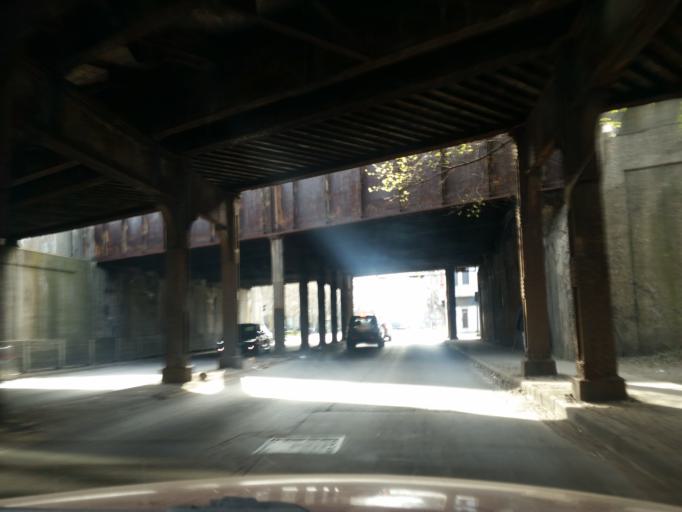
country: US
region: Ohio
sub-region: Cuyahoga County
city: East Cleveland
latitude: 41.5231
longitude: -81.5923
